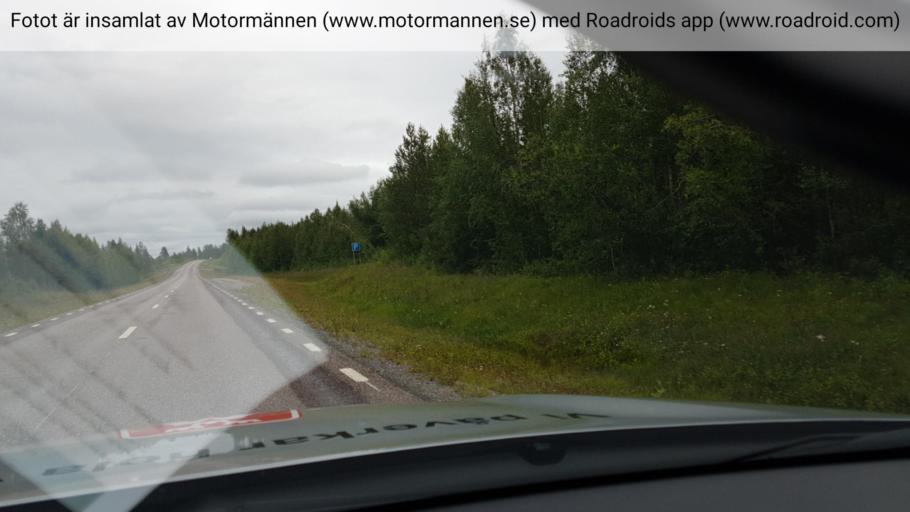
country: SE
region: Norrbotten
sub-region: Gallivare Kommun
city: Gaellivare
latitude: 67.0704
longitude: 21.5125
